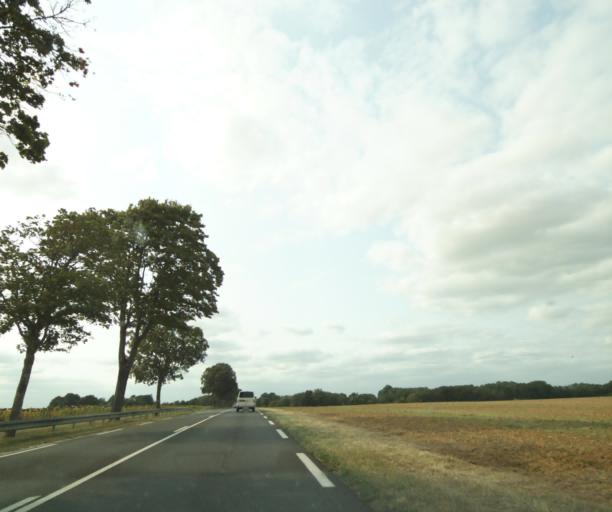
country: FR
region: Centre
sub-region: Departement d'Indre-et-Loire
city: Reignac-sur-Indre
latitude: 47.2286
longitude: 0.8779
